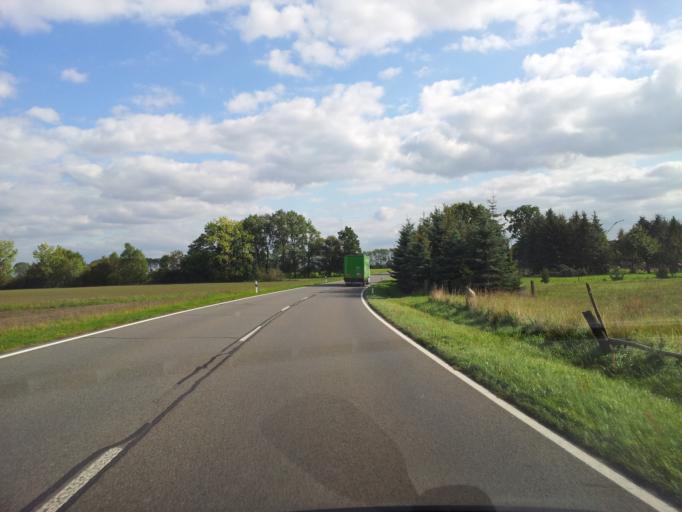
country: DE
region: Brandenburg
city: Sallgast
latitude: 51.6111
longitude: 13.8576
